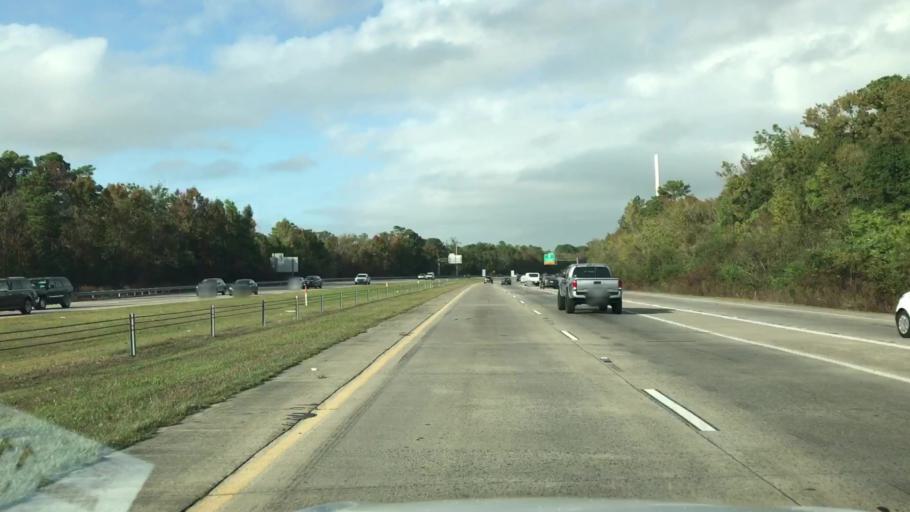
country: US
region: South Carolina
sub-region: Berkeley County
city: Hanahan
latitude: 32.8727
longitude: -80.0268
